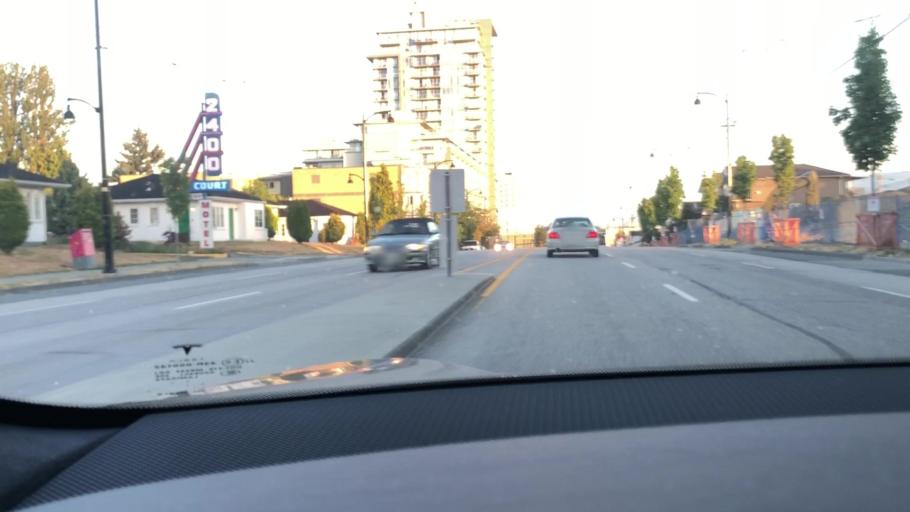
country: CA
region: British Columbia
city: Vancouver
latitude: 49.2407
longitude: -123.0554
